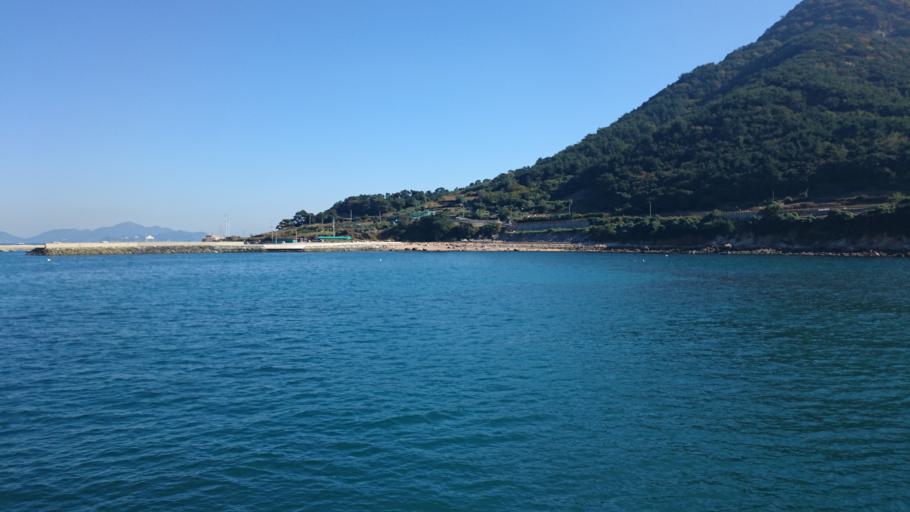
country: KR
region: Gyeongsangnam-do
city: Kyosai
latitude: 34.7175
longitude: 128.4548
